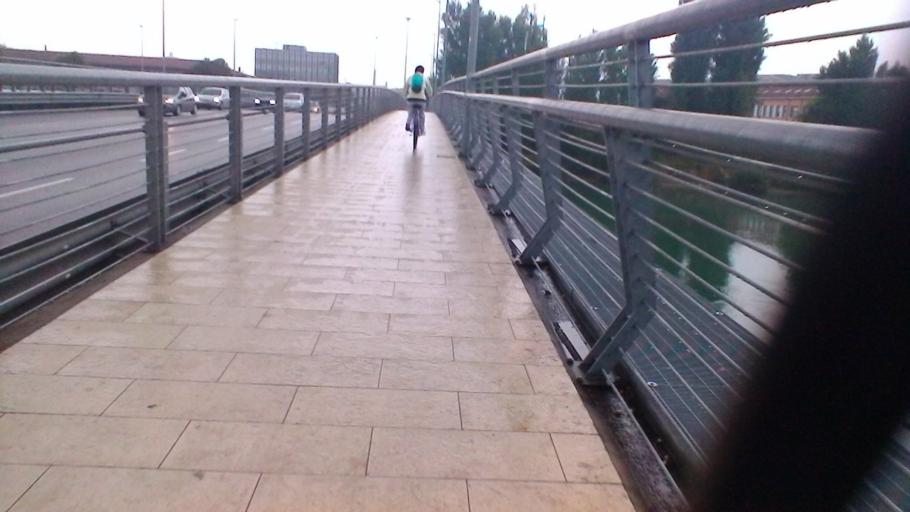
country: IT
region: Veneto
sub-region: Provincia di Verona
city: Verona
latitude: 45.4300
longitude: 10.9965
